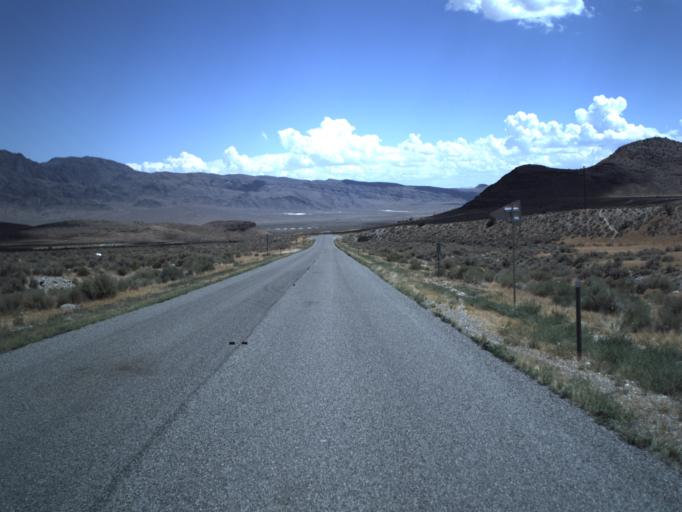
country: US
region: Utah
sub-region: Beaver County
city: Milford
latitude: 39.0879
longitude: -113.5502
